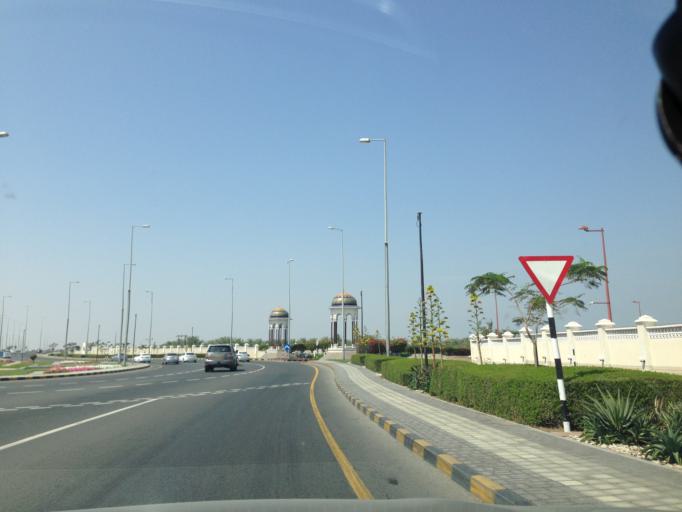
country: OM
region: Muhafazat Masqat
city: As Sib al Jadidah
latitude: 23.6629
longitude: 58.1717
